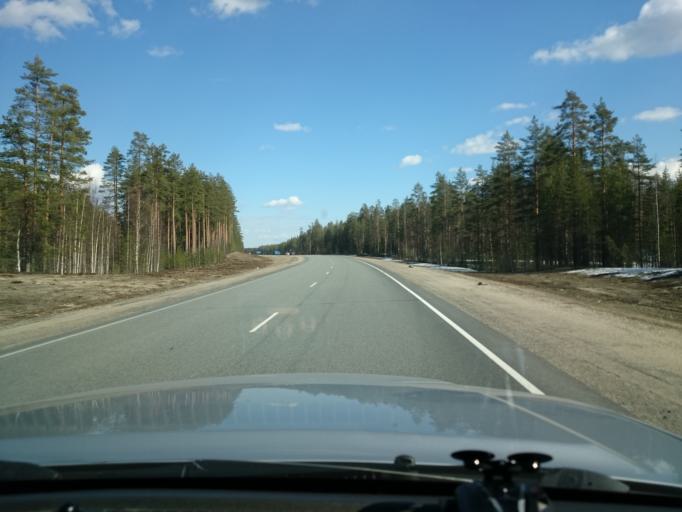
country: RU
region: Republic of Karelia
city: Pryazha
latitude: 61.4603
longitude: 33.3202
